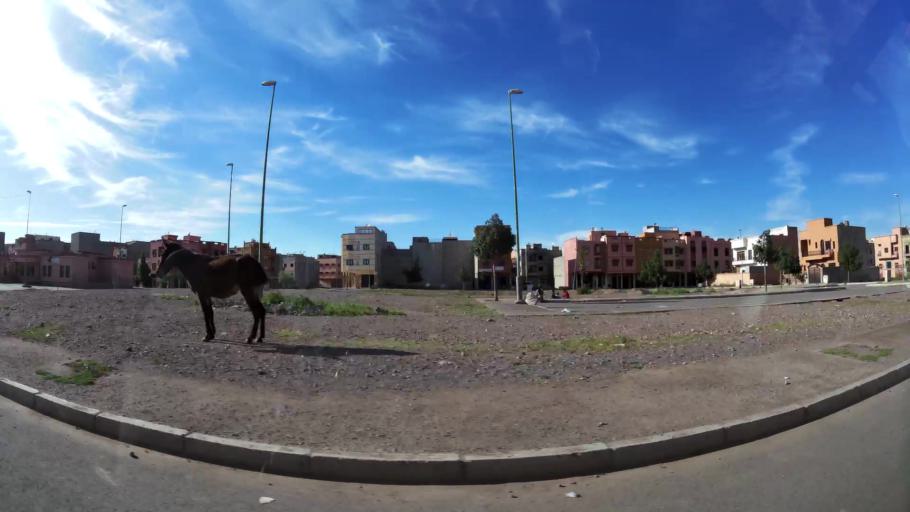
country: MA
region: Marrakech-Tensift-Al Haouz
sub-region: Marrakech
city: Marrakesh
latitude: 31.6882
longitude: -8.0655
